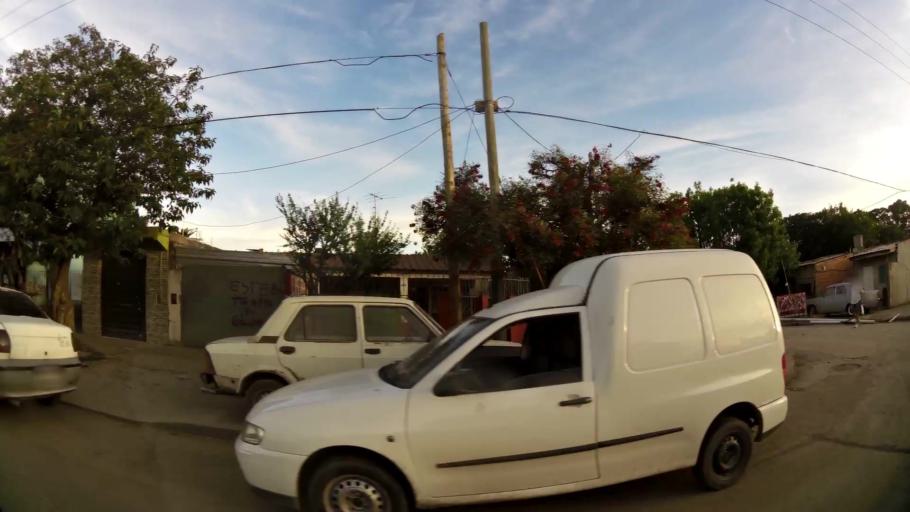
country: AR
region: Buenos Aires
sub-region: Partido de Almirante Brown
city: Adrogue
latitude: -34.7762
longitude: -58.3292
